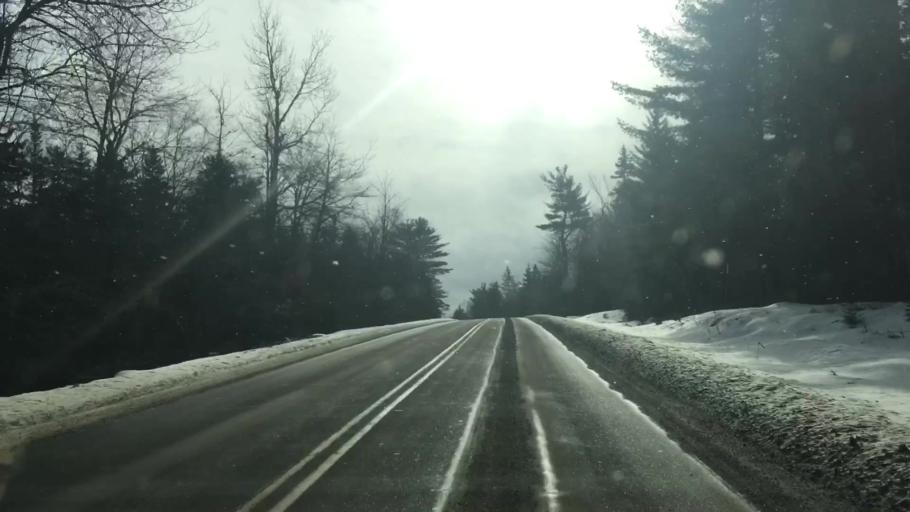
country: US
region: Maine
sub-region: Washington County
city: Calais
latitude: 45.0663
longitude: -67.3303
